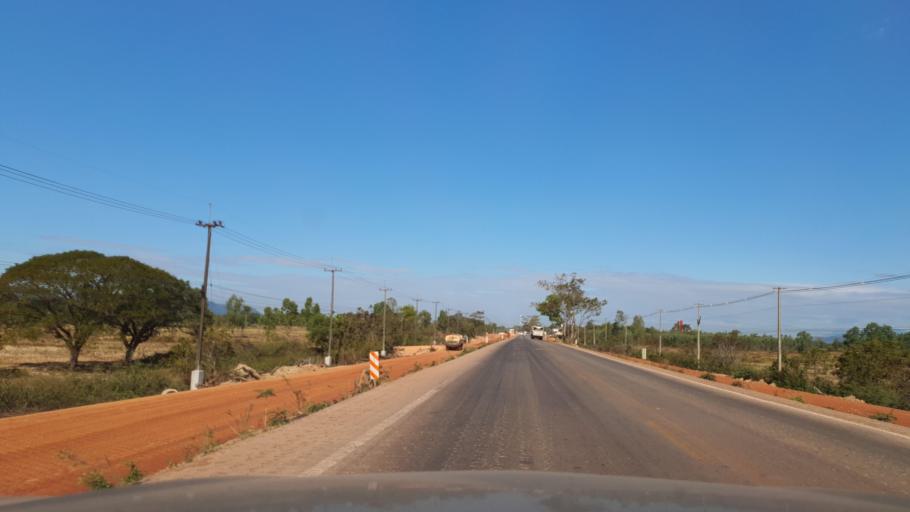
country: TH
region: Nakhon Phanom
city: Ban Phaeng
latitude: 17.9030
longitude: 104.2331
